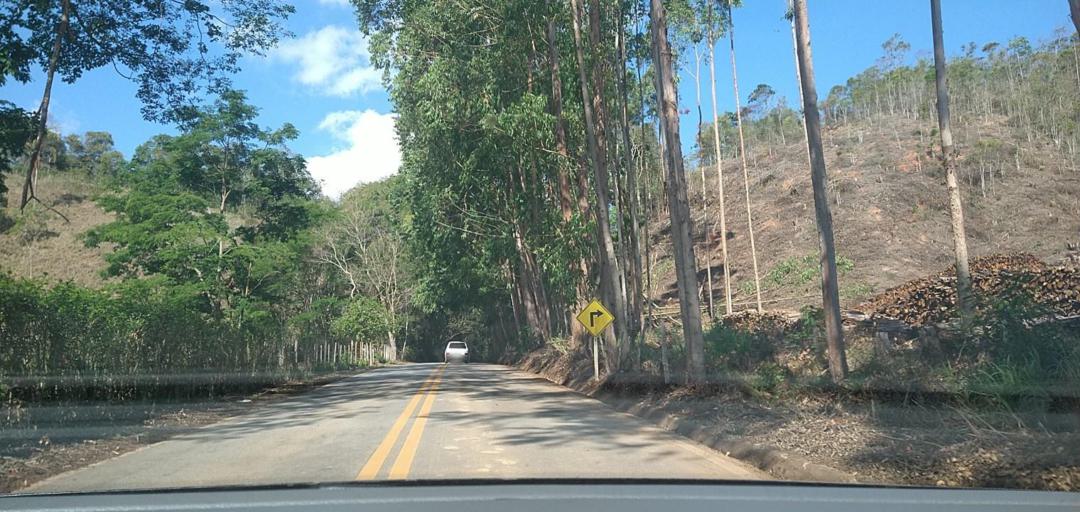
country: BR
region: Minas Gerais
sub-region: Alvinopolis
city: Alvinopolis
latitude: -20.0355
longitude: -43.0387
